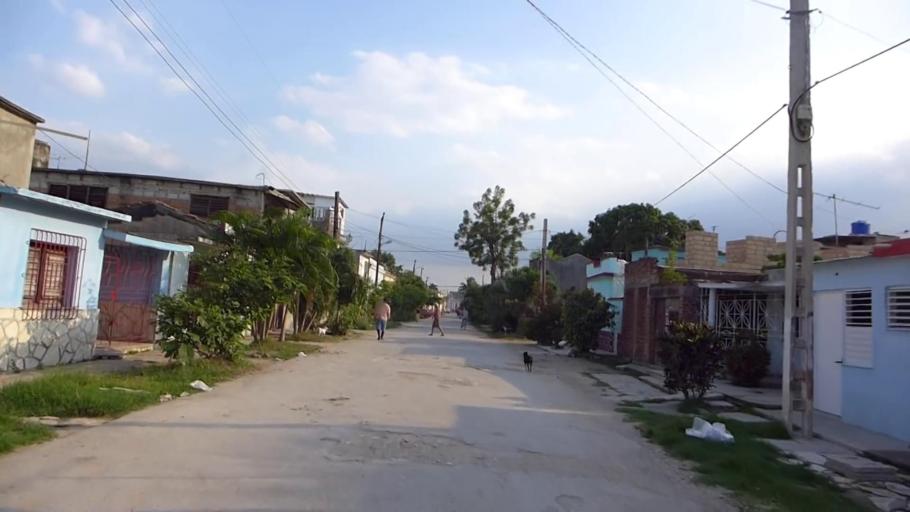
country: CU
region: Camaguey
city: Camaguey
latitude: 21.3865
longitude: -77.9098
